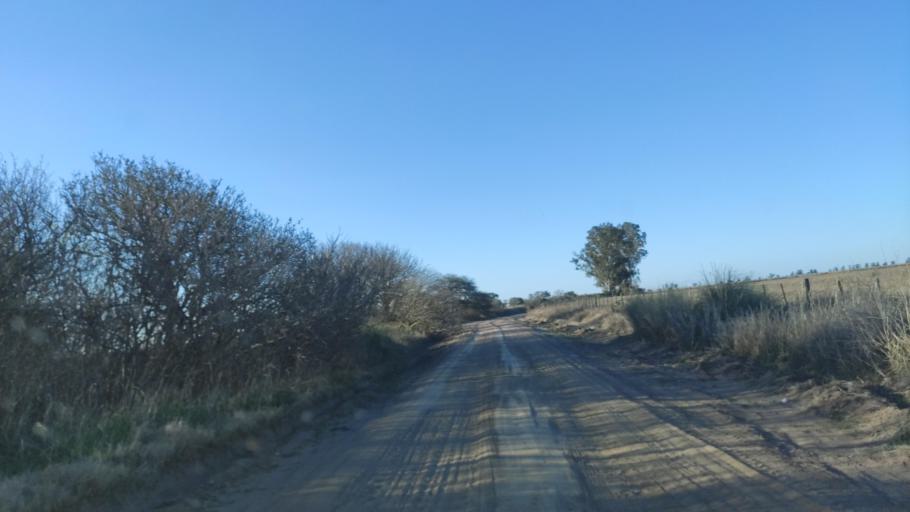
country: AR
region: Cordoba
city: Monte Buey
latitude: -32.8562
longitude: -62.3850
